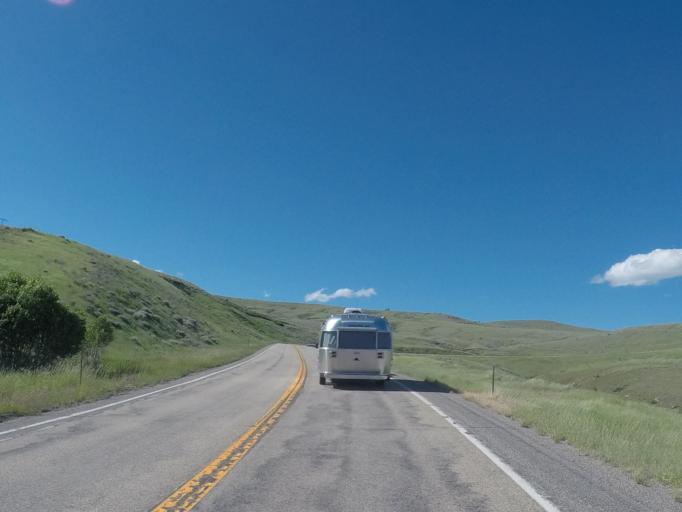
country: US
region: Montana
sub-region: Carbon County
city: Red Lodge
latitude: 45.1692
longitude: -109.2149
